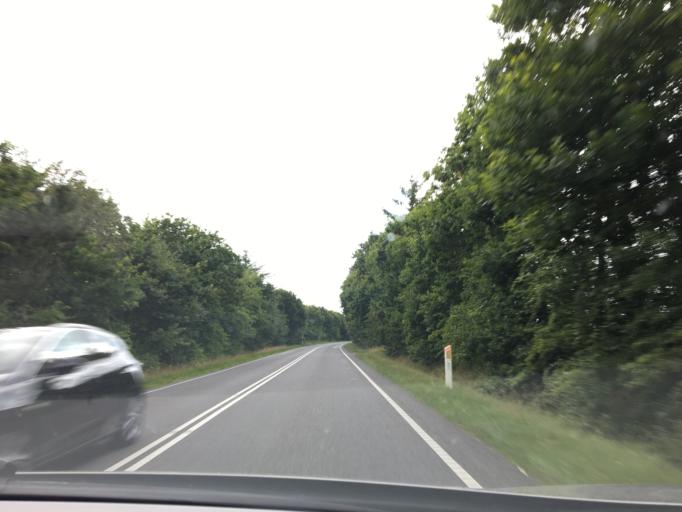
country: DK
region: South Denmark
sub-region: Varde Kommune
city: Oksbol
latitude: 55.7041
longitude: 8.3119
